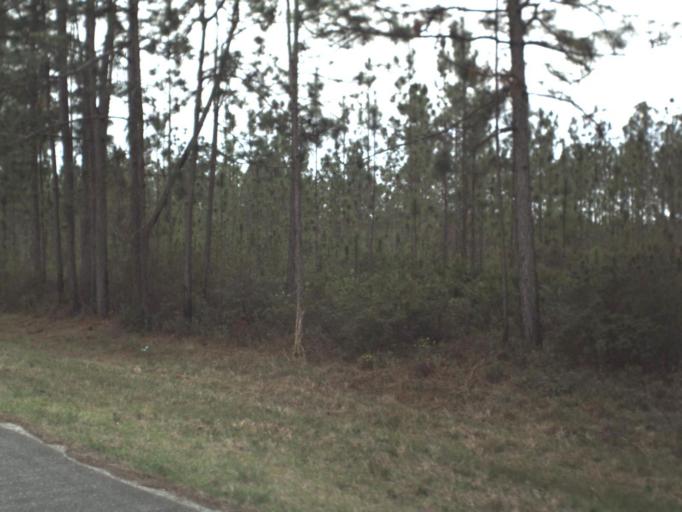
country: US
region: Florida
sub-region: Gadsden County
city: Midway
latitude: 30.3595
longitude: -84.5318
